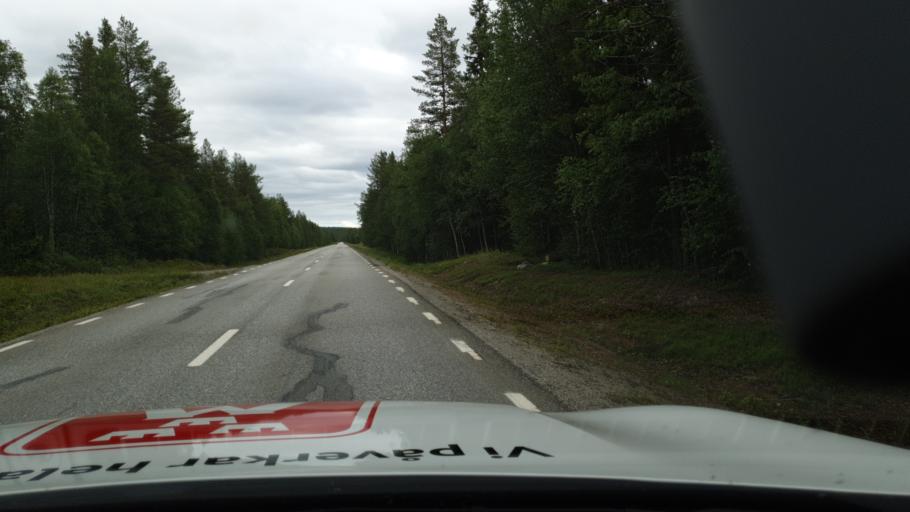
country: SE
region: Vaesterbotten
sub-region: Lycksele Kommun
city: Soderfors
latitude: 64.6940
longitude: 17.7561
